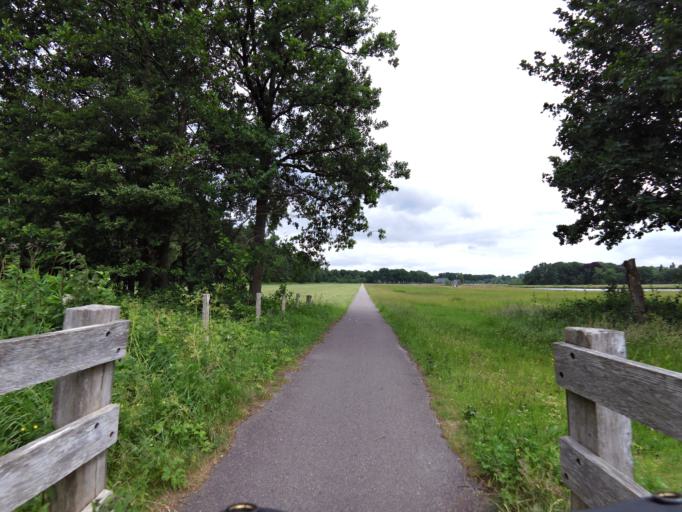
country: NL
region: North Brabant
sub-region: Gemeente Breda
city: Breda
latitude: 51.5535
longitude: 4.7853
